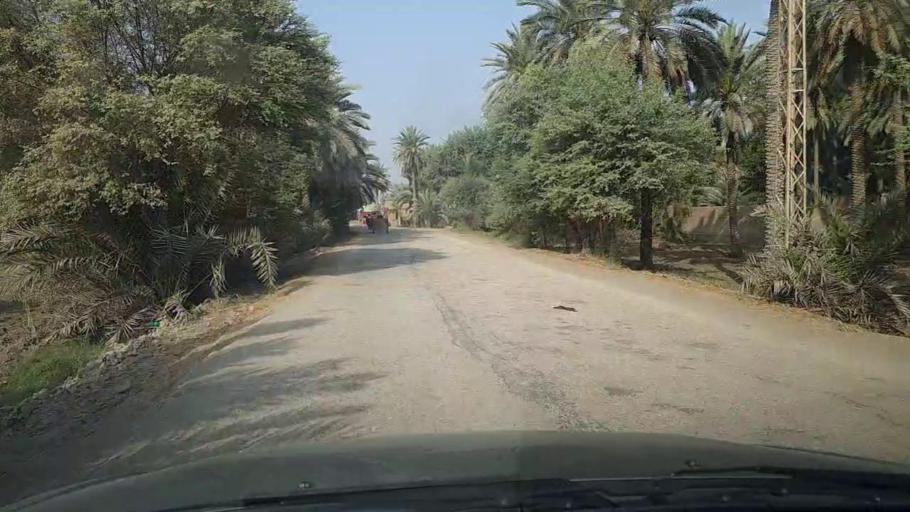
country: PK
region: Sindh
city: Pir jo Goth
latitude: 27.5586
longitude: 68.5631
